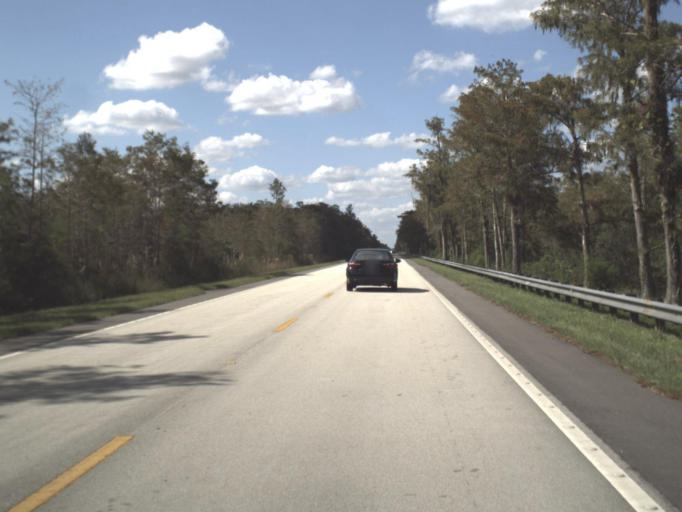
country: US
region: Florida
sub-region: Miami-Dade County
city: Kendall West
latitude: 25.8220
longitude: -80.8924
